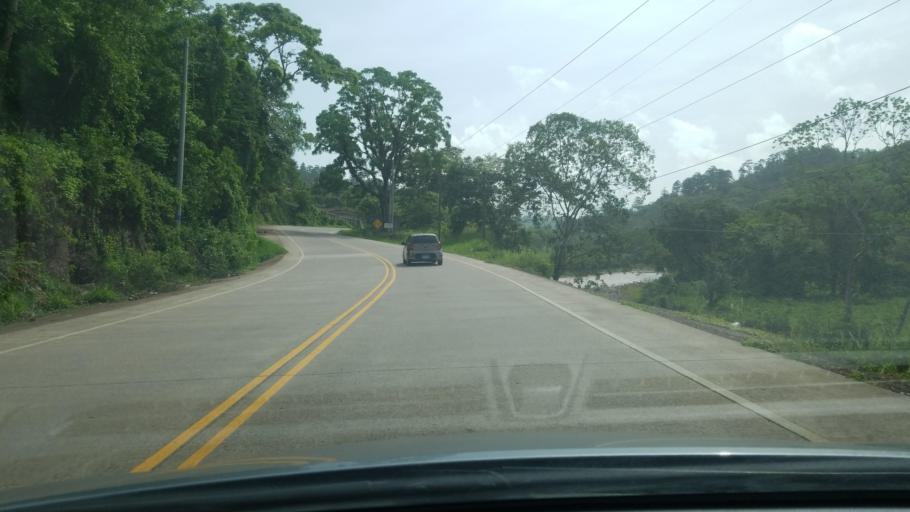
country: HN
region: Copan
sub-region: Santa Rita
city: Santa Rita, Copan
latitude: 14.8734
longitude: -89.0508
